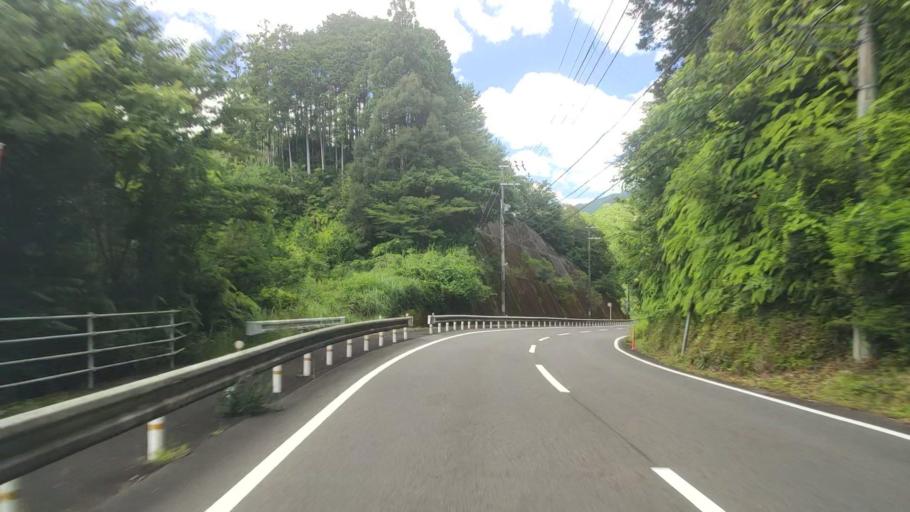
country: JP
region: Mie
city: Owase
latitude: 33.9544
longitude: 136.0690
